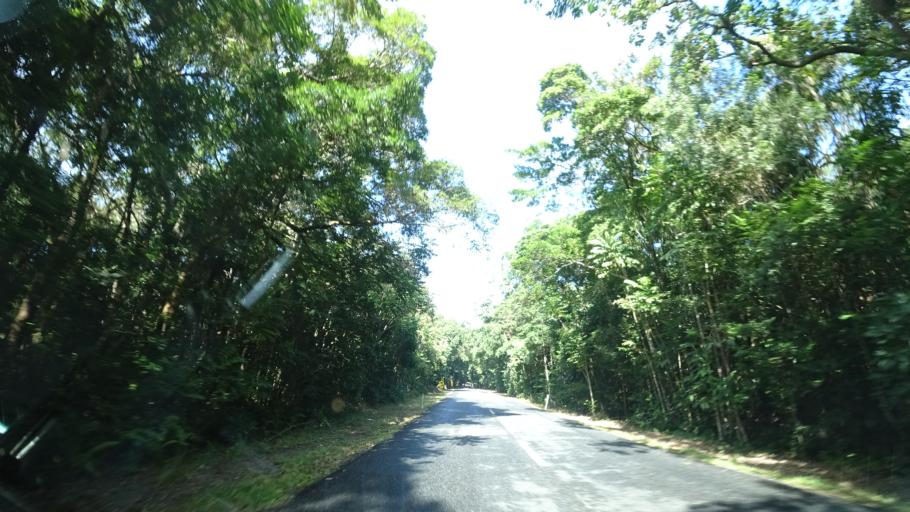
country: AU
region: Queensland
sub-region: Cairns
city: Port Douglas
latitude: -16.1341
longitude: 145.4516
